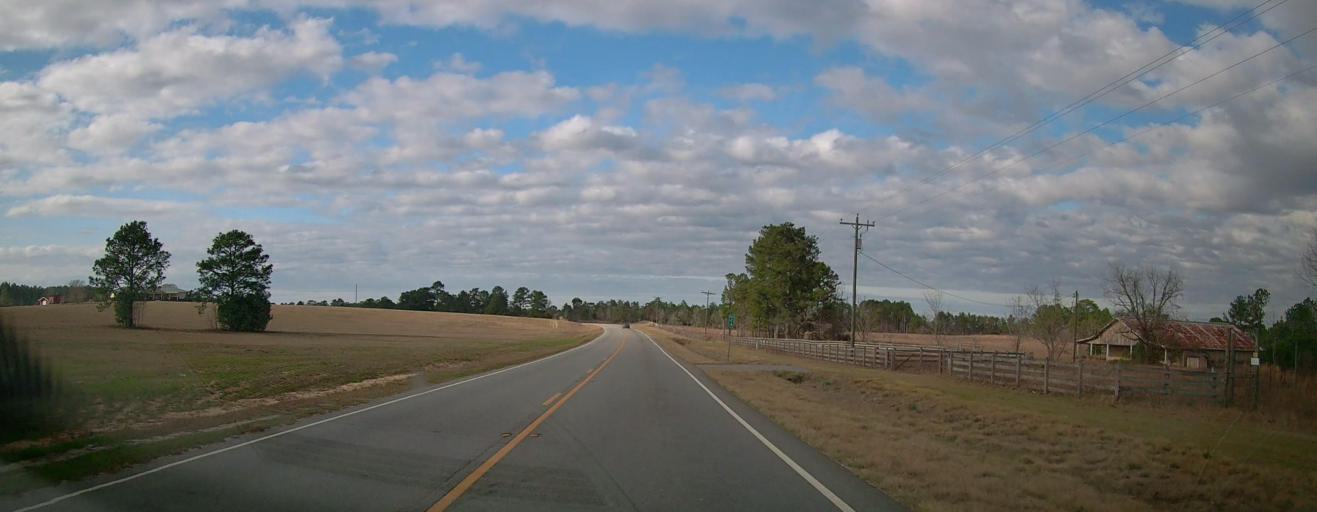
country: US
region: Georgia
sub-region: Marion County
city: Buena Vista
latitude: 32.4809
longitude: -84.5453
